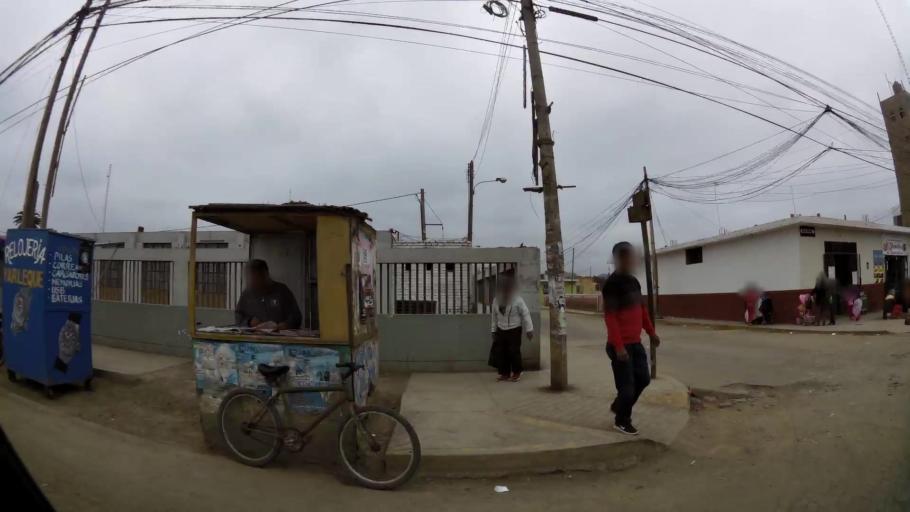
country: PE
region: Lima
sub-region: Barranca
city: Paramonga
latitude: -10.6765
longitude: -77.8190
